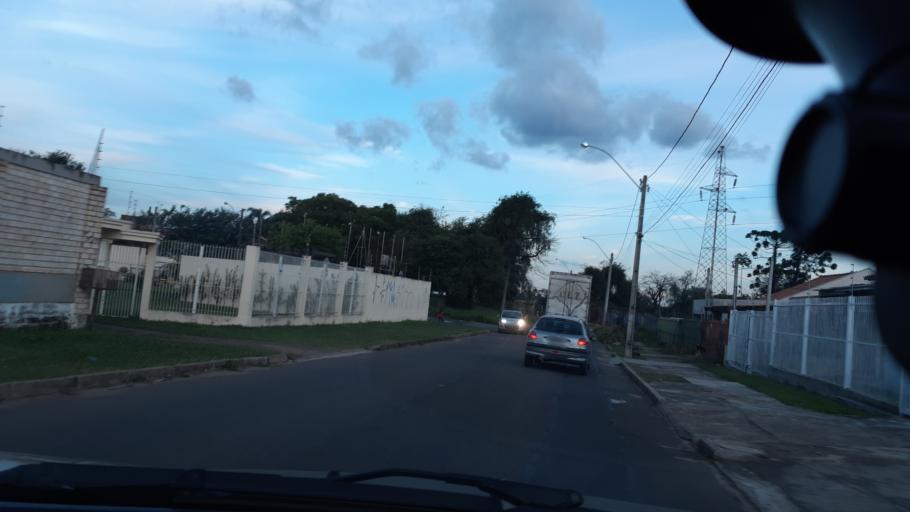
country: BR
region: Rio Grande do Sul
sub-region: Sapucaia Do Sul
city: Sapucaia
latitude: -29.8450
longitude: -51.1478
